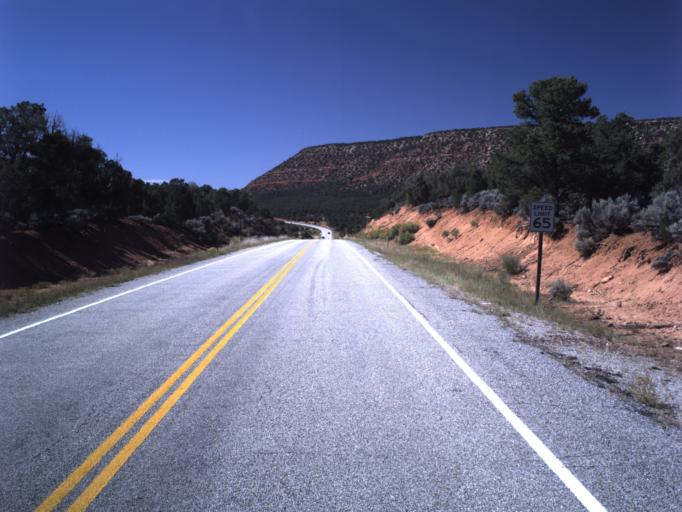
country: US
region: Utah
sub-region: San Juan County
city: Blanding
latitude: 37.5802
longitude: -109.8873
